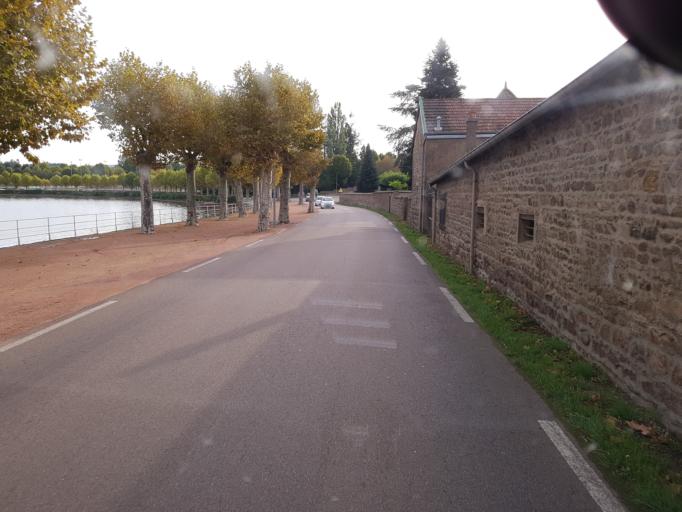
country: FR
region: Bourgogne
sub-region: Departement de Saone-et-Loire
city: La Clayette
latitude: 46.2909
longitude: 4.3143
